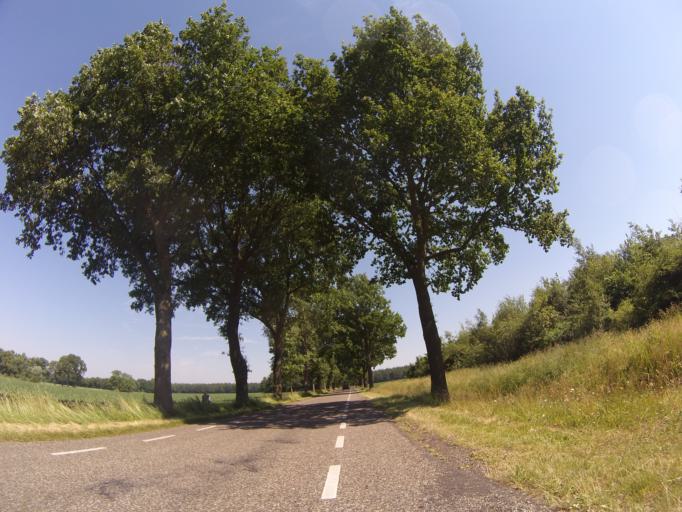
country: NL
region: Drenthe
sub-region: Gemeente Coevorden
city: Sleen
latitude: 52.8145
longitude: 6.7414
